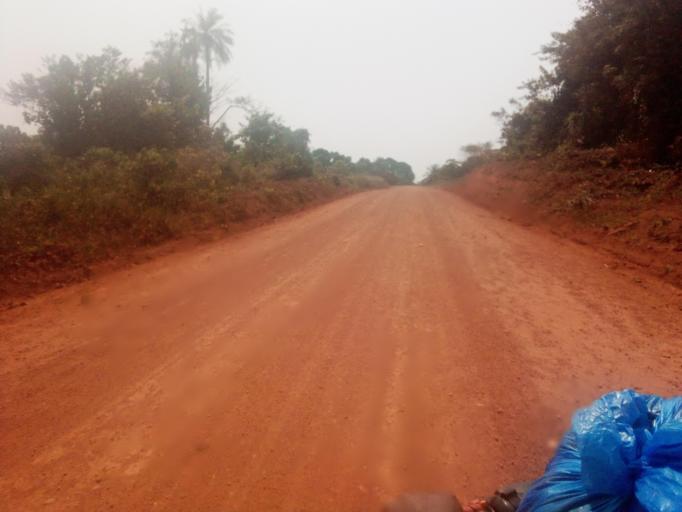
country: SL
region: Southern Province
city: Sumbuya
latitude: 7.6640
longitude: -11.9905
